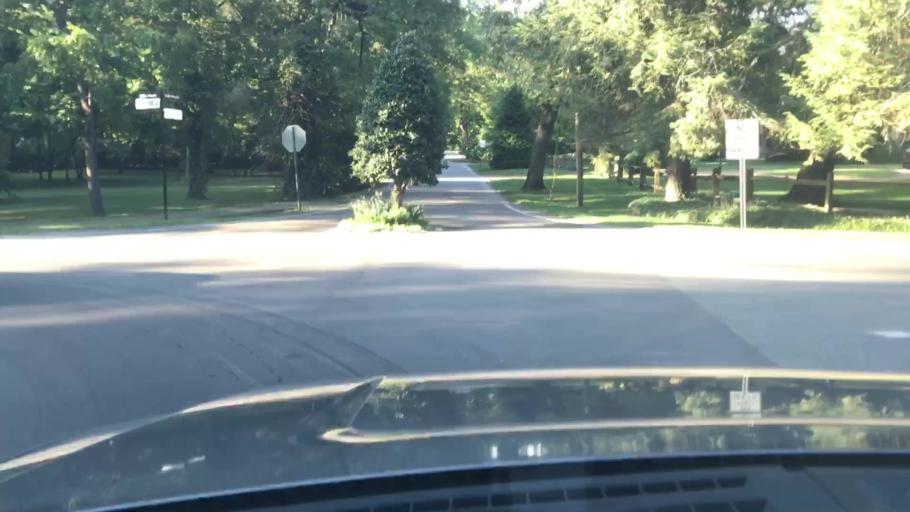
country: US
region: Tennessee
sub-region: Davidson County
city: Belle Meade
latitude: 36.1159
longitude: -86.8478
